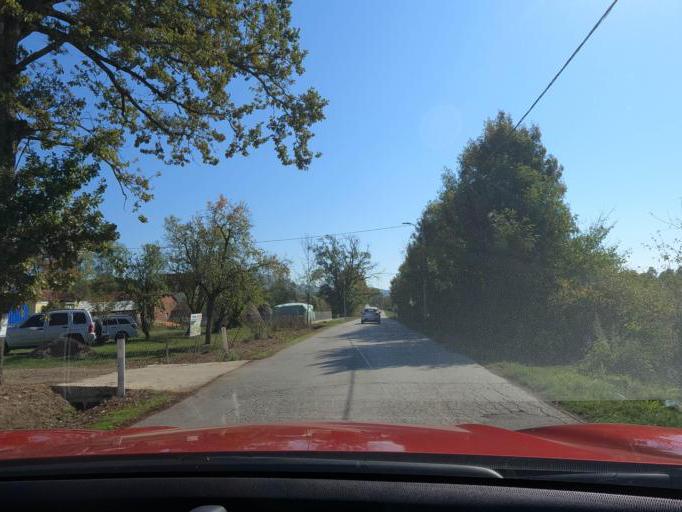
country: RS
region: Central Serbia
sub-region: Raski Okrug
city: Kraljevo
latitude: 43.7557
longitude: 20.6909
